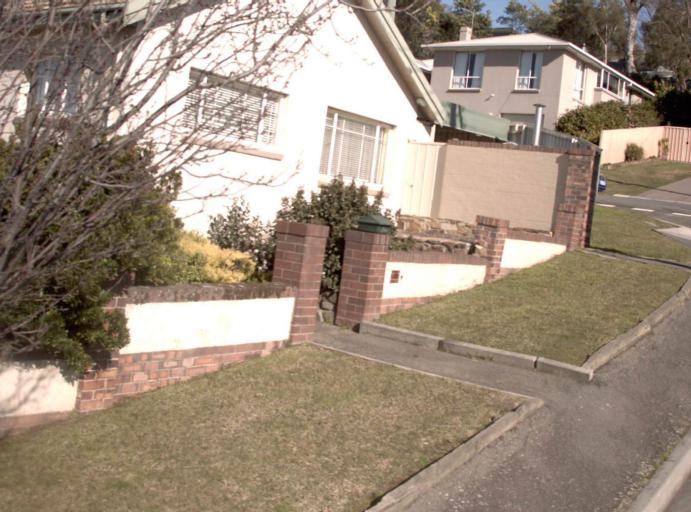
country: AU
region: Tasmania
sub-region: Launceston
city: Summerhill
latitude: -41.4734
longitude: 147.1568
